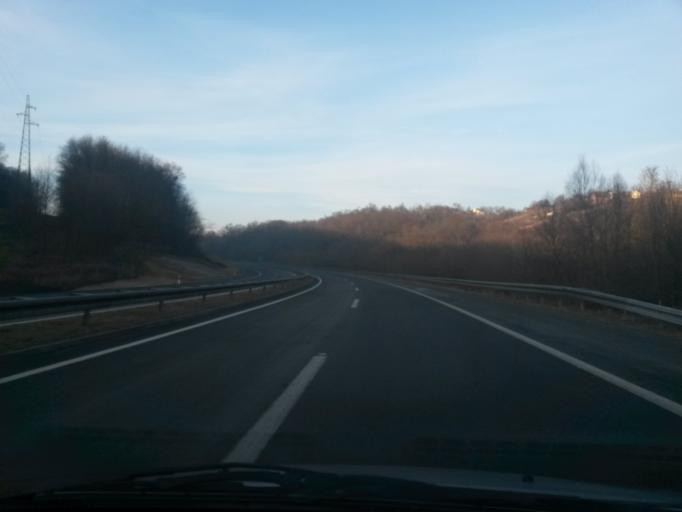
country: HR
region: Varazdinska
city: Jalzabet
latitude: 46.2377
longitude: 16.4109
